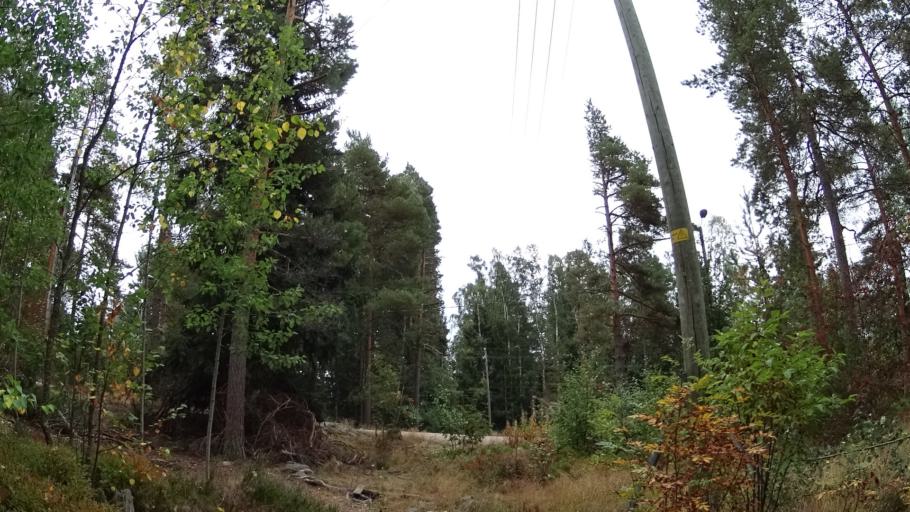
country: FI
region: Uusimaa
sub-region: Helsinki
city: Kilo
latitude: 60.1947
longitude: 24.7596
